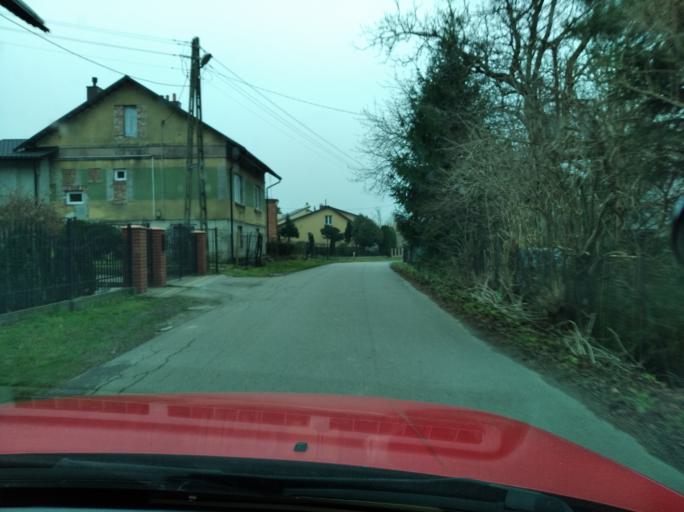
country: PL
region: Subcarpathian Voivodeship
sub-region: Powiat jaroslawski
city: Pawlosiow
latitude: 49.9671
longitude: 22.6477
